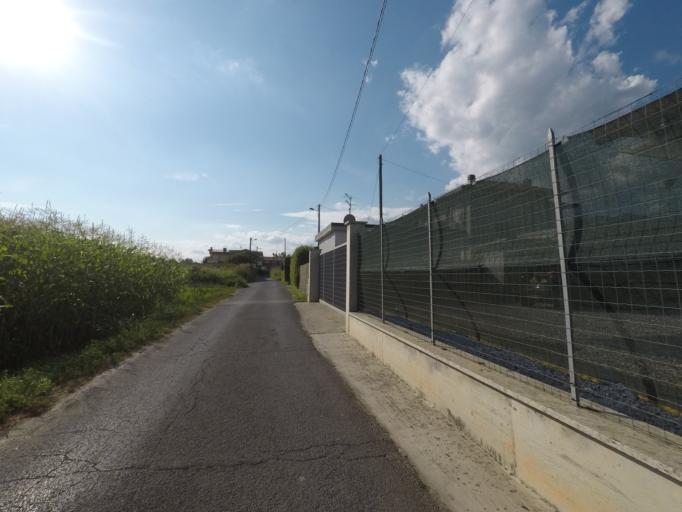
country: IT
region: Tuscany
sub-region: Provincia di Massa-Carrara
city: Capanne-Prato-Cinquale
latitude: 44.0131
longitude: 10.1451
